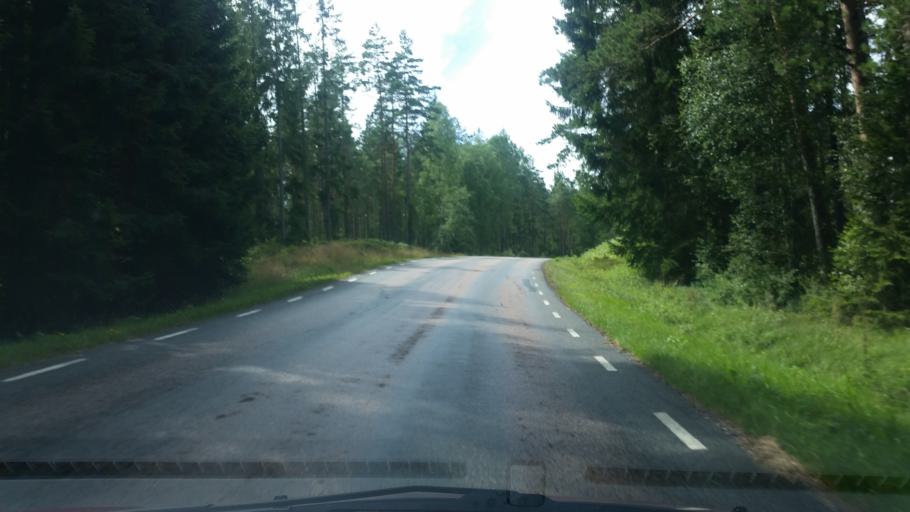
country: SE
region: Joenkoeping
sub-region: Gislaveds Kommun
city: Reftele
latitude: 57.2167
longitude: 13.6283
